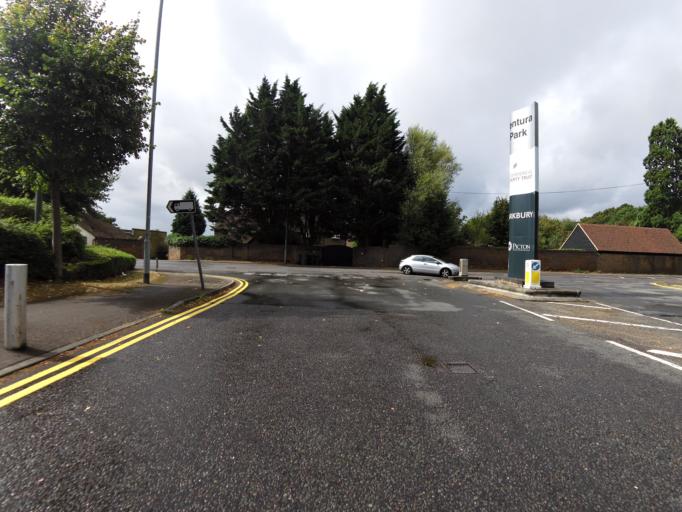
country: GB
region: England
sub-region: Hertfordshire
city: Radlett
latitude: 51.7070
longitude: -0.3295
